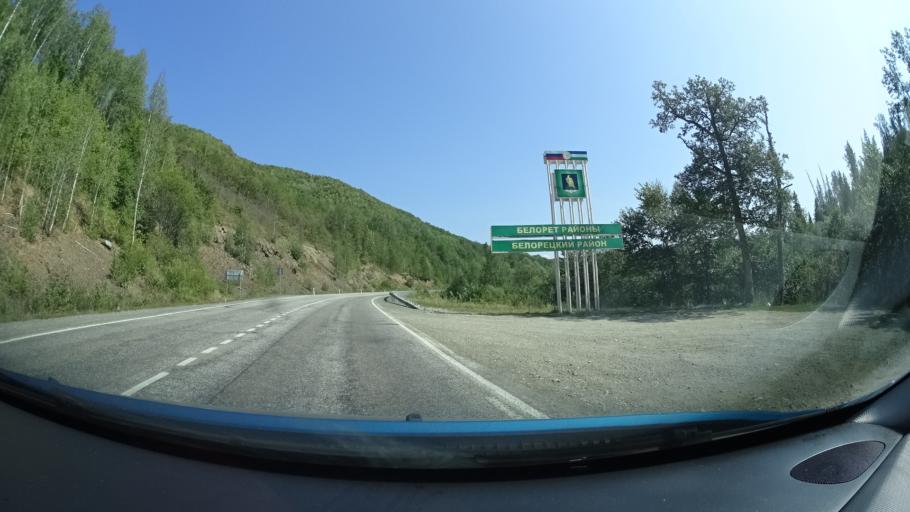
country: RU
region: Bashkortostan
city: Inzer
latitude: 54.3380
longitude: 57.1452
